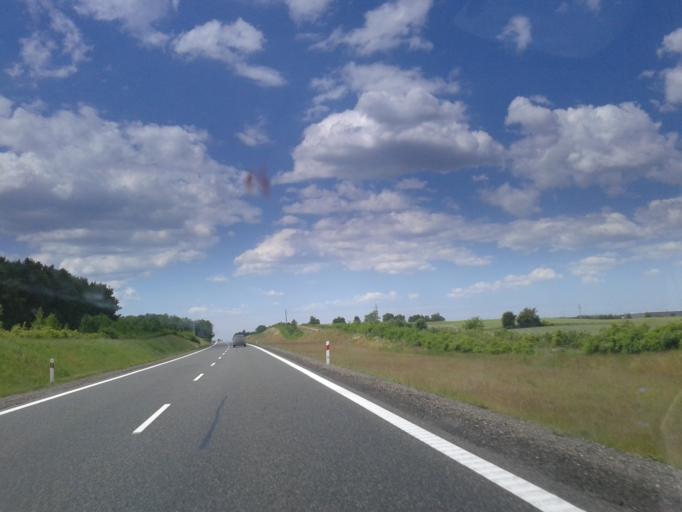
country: PL
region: Pomeranian Voivodeship
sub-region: Powiat chojnicki
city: Chojnice
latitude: 53.6831
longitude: 17.5277
